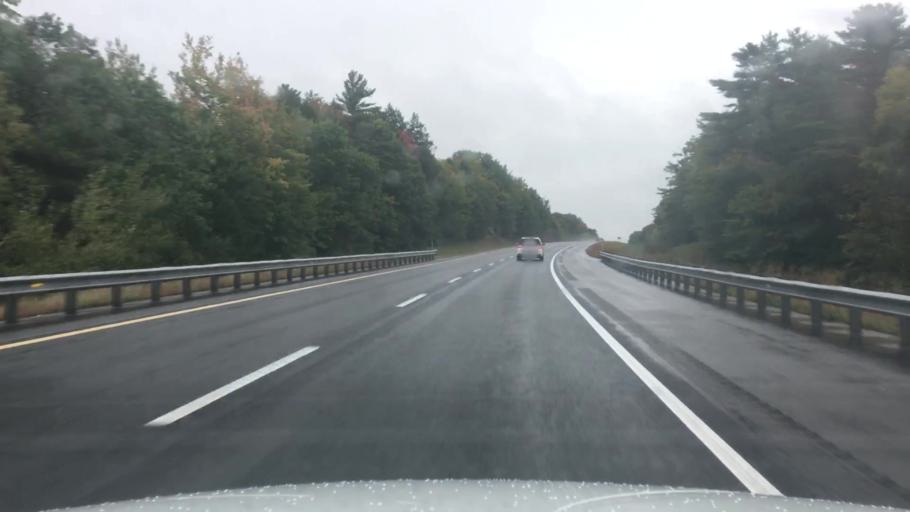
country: US
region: Maine
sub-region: Sagadahoc County
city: Topsham
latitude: 43.9936
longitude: -69.9373
